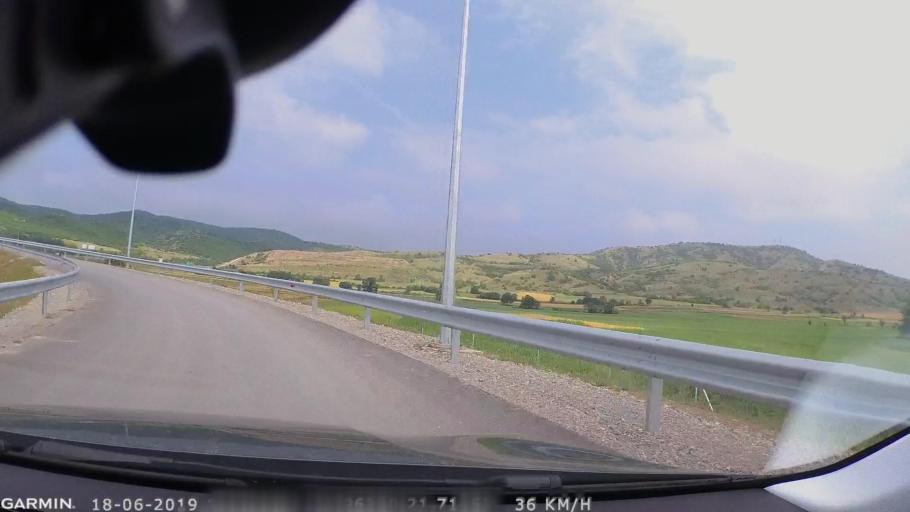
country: MK
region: Petrovec
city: Sredno Konjare
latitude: 41.9441
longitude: 21.8074
